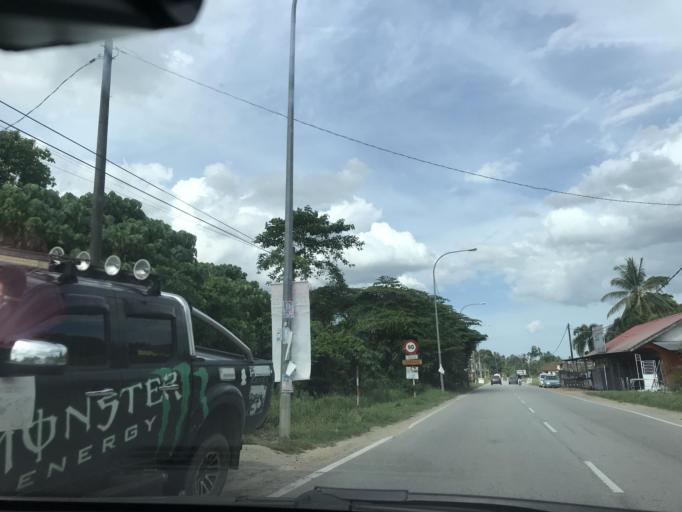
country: MY
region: Kelantan
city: Kampung Lemal
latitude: 6.0336
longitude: 102.1610
